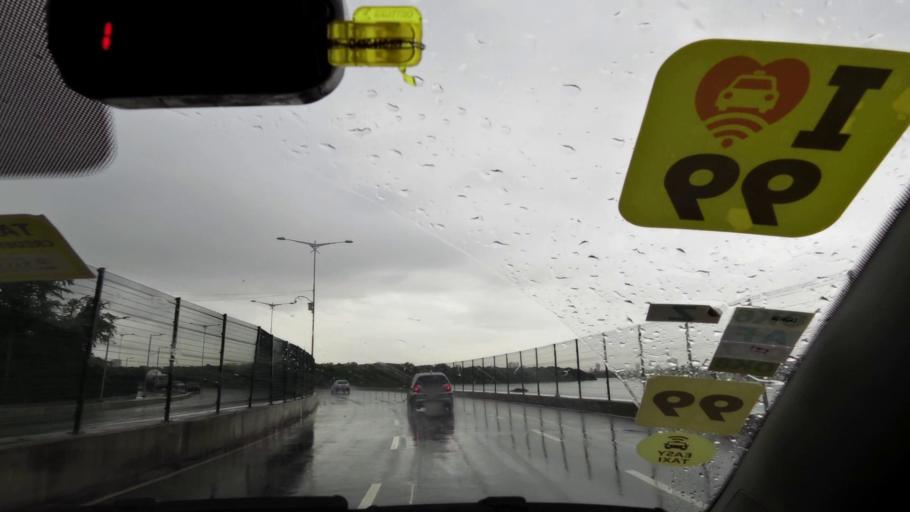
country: BR
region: Pernambuco
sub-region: Recife
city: Recife
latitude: -8.1208
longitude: -34.9010
